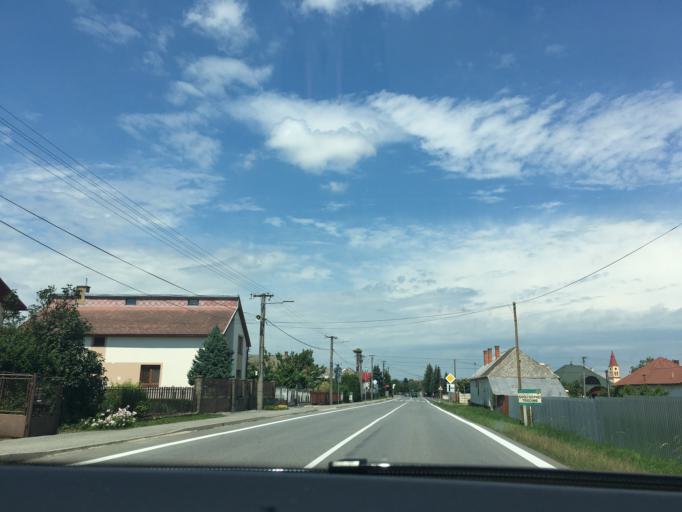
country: SK
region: Presovsky
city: Vranov nad Topl'ou
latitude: 48.8177
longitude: 21.6873
